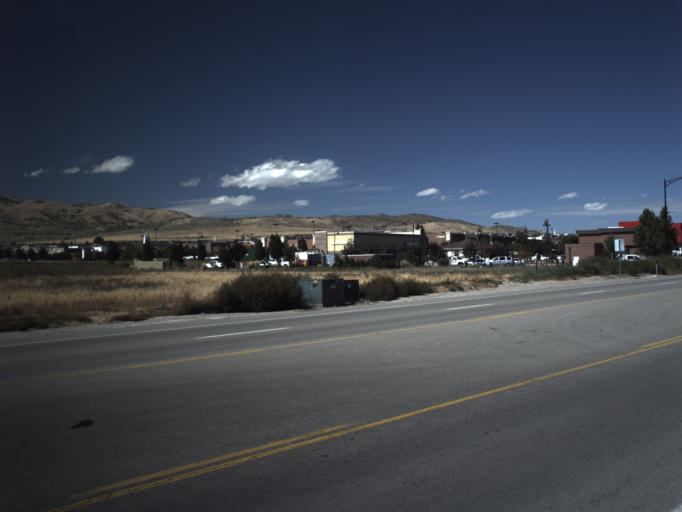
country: US
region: Utah
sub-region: Utah County
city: Saratoga Springs
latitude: 40.3857
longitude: -111.9163
